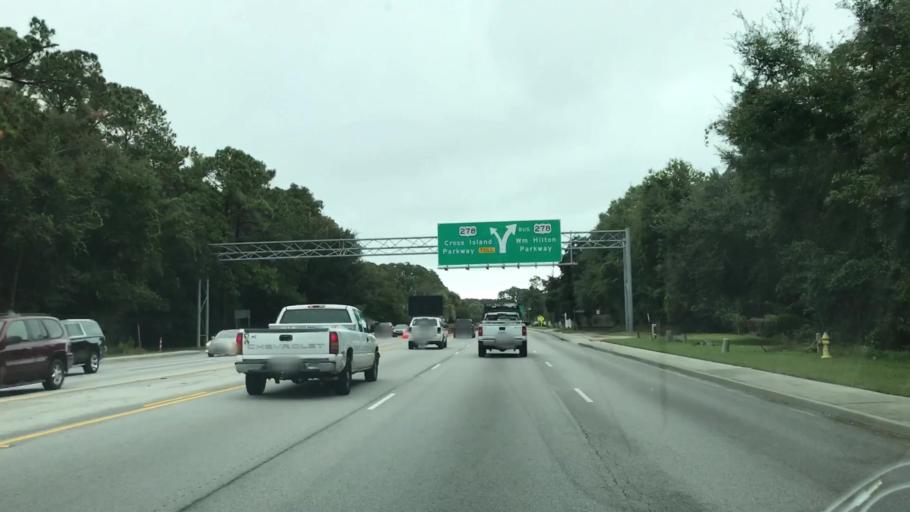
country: US
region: South Carolina
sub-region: Beaufort County
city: Hilton Head Island
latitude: 32.2164
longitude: -80.7528
